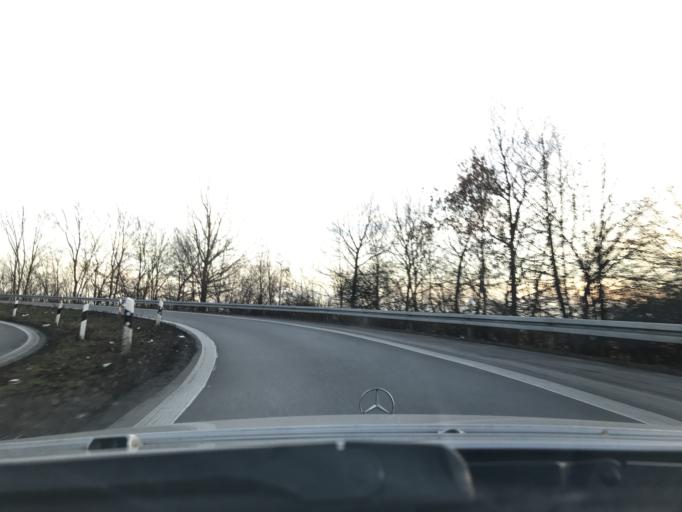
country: DE
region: North Rhine-Westphalia
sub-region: Regierungsbezirk Arnsberg
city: Werl
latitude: 51.5680
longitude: 7.8841
